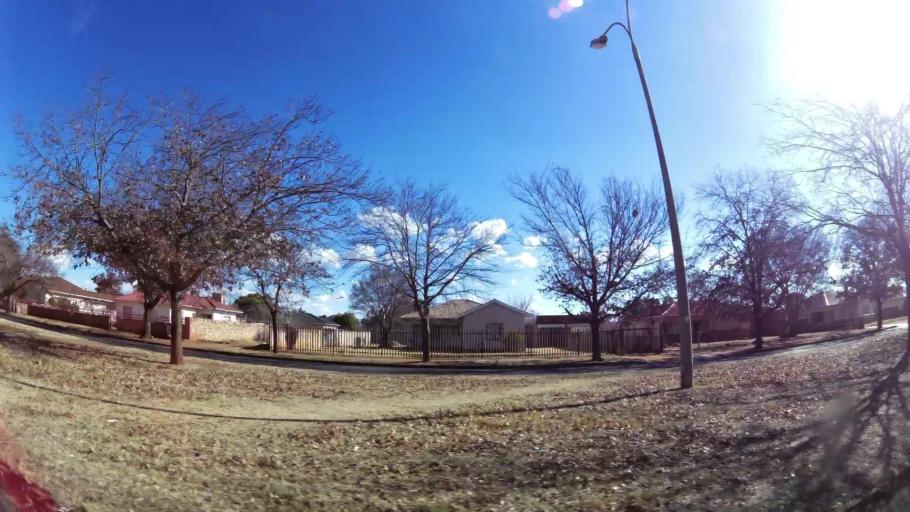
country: ZA
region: Gauteng
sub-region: West Rand District Municipality
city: Carletonville
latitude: -26.3648
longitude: 27.3937
